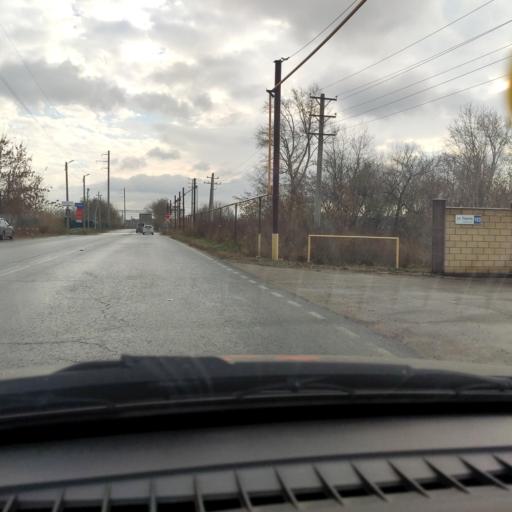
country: RU
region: Samara
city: Zhigulevsk
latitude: 53.5275
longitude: 49.4768
